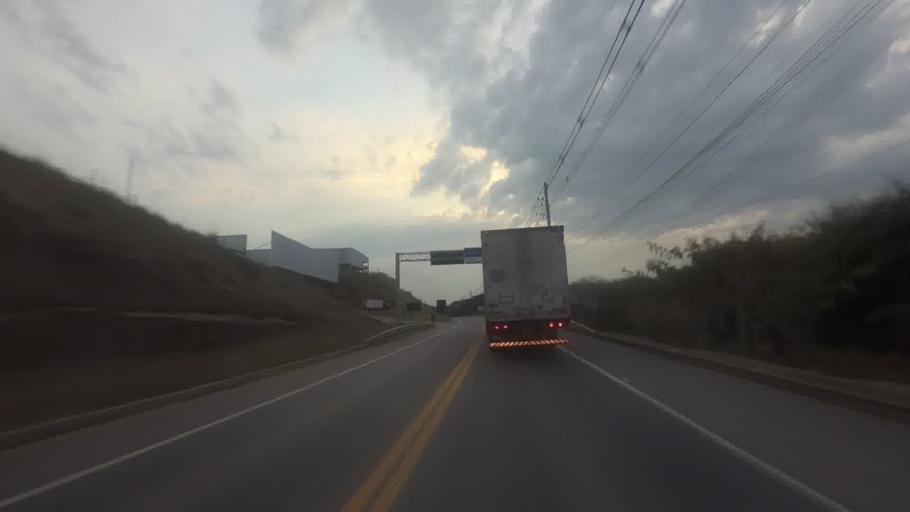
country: BR
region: Minas Gerais
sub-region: Alem Paraiba
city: Alem Paraiba
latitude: -21.8813
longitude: -42.6861
